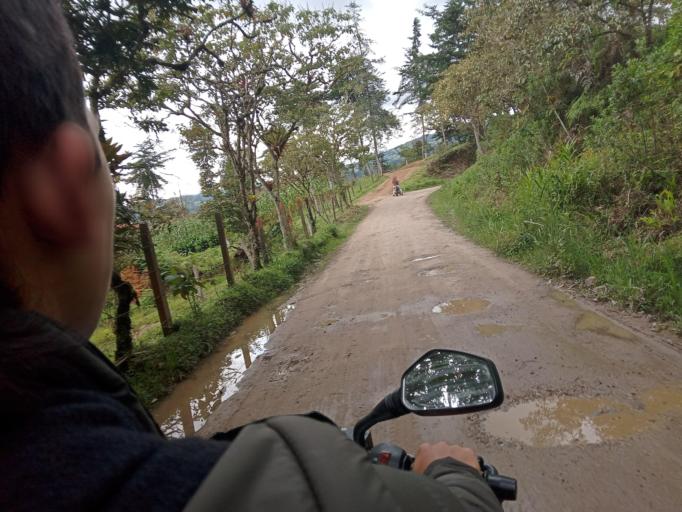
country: CO
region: Cundinamarca
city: Tenza
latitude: 5.1012
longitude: -73.4273
